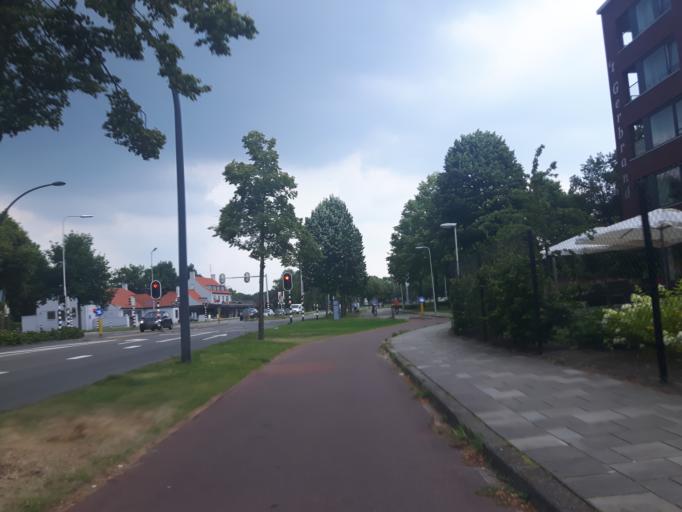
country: NL
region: Overijssel
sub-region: Gemeente Hengelo
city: Hengelo
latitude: 52.2751
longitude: 6.8226
